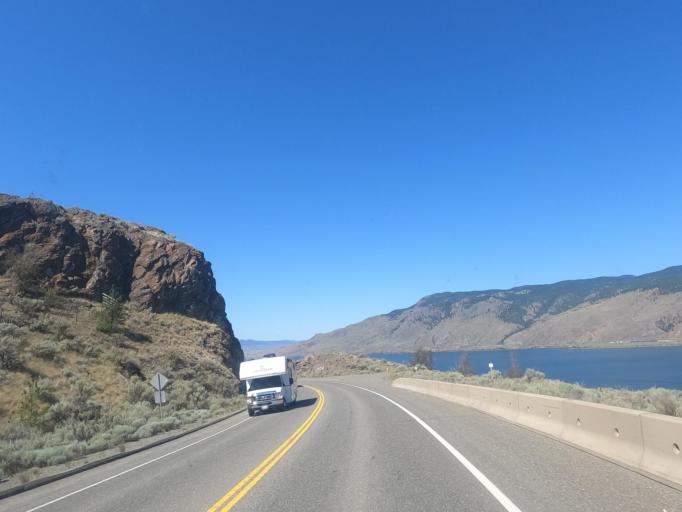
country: CA
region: British Columbia
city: Logan Lake
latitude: 50.7650
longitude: -120.7760
